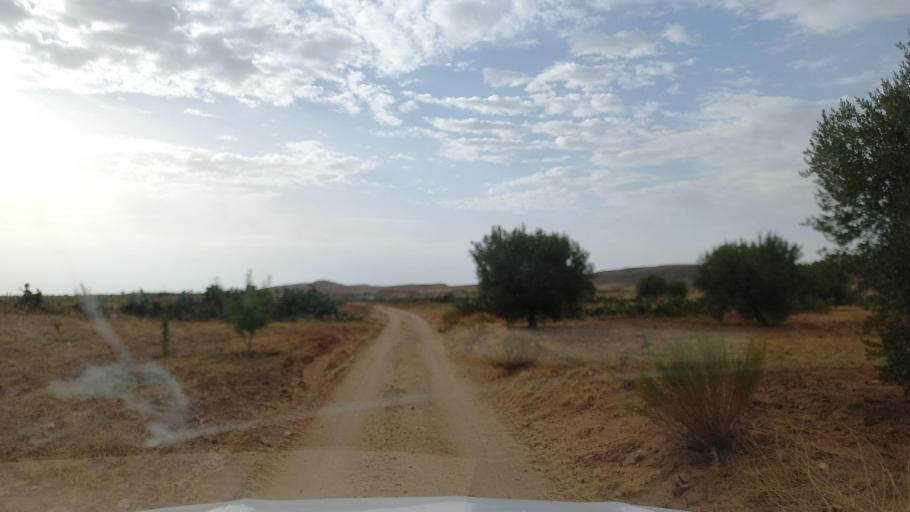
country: TN
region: Al Qasrayn
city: Kasserine
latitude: 35.1894
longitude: 9.0514
